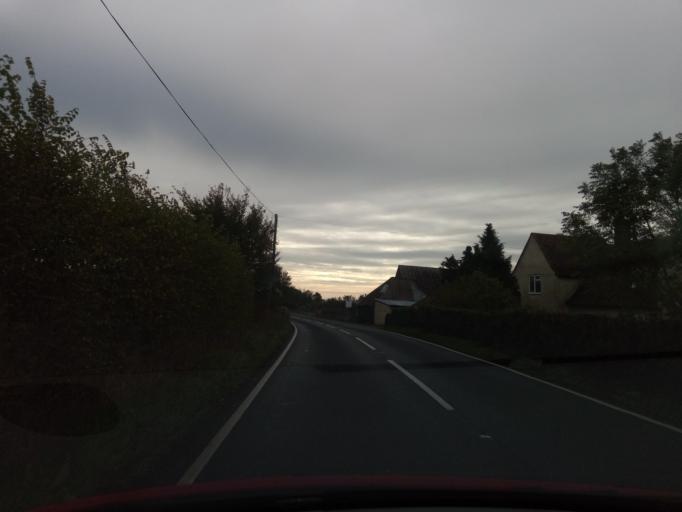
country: GB
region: England
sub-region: Essex
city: West Mersea
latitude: 51.8073
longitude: 0.8999
